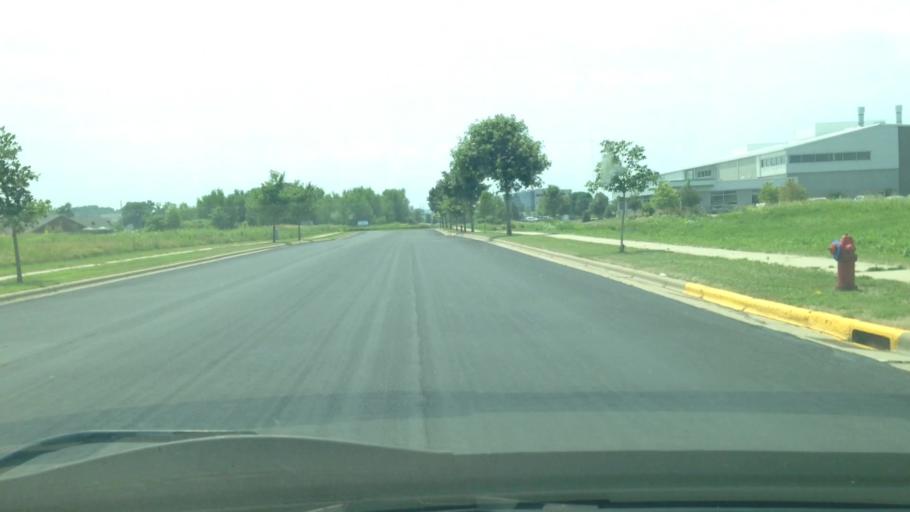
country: US
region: Wisconsin
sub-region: Dane County
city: Middleton
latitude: 43.1081
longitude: -89.5212
